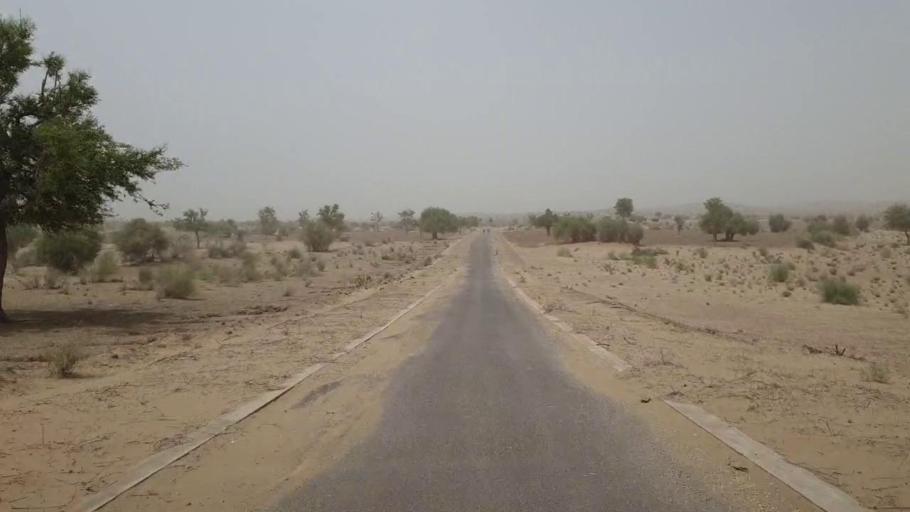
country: PK
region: Sindh
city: Islamkot
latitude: 24.8066
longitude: 70.5272
